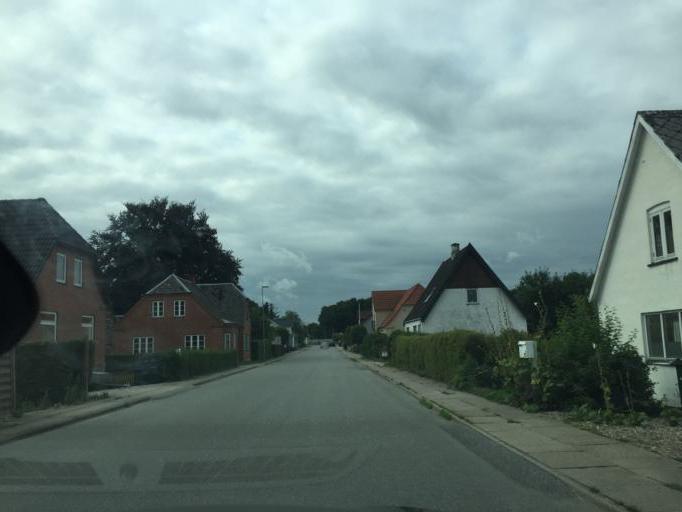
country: DK
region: South Denmark
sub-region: Assens Kommune
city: Vissenbjerg
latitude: 55.3669
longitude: 10.1456
